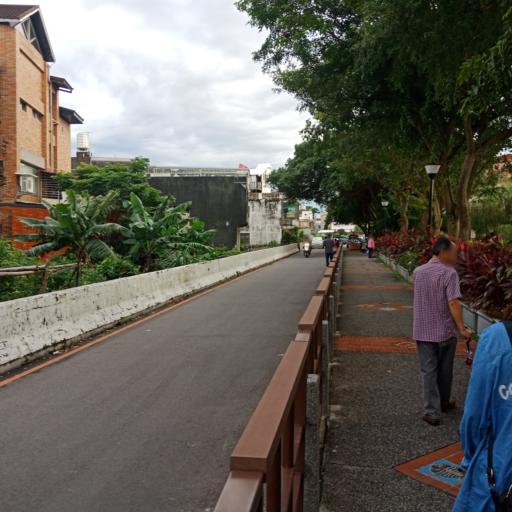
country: TW
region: Taiwan
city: Daxi
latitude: 24.8624
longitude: 121.2119
